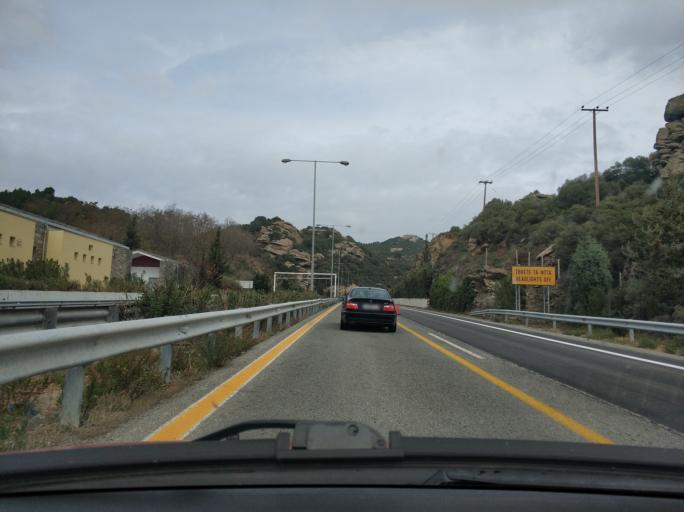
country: GR
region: East Macedonia and Thrace
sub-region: Nomos Kavalas
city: Palaio Tsifliki
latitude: 40.9118
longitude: 24.3587
